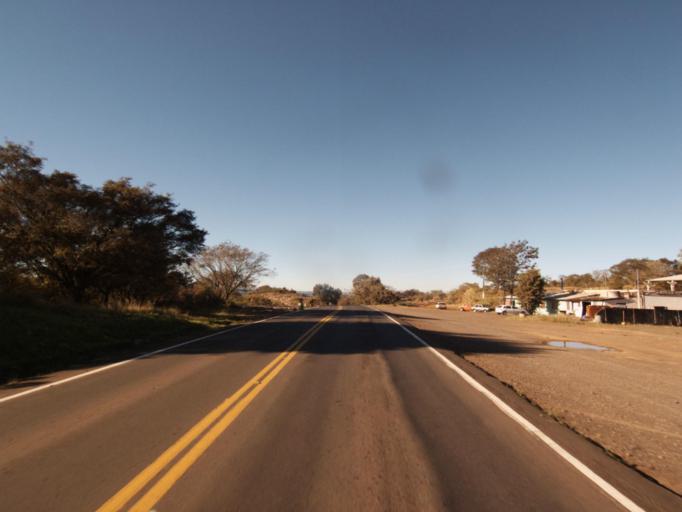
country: AR
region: Misiones
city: Bernardo de Irigoyen
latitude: -26.4968
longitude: -53.5032
